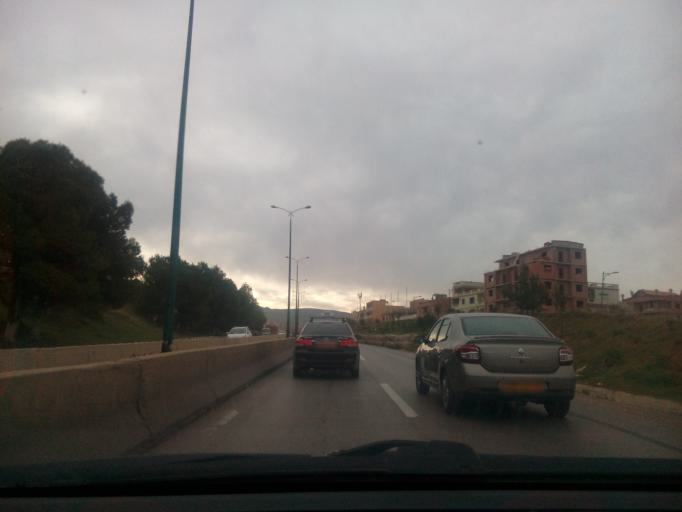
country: DZ
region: Tlemcen
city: Mansoura
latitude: 34.8907
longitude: -1.3555
